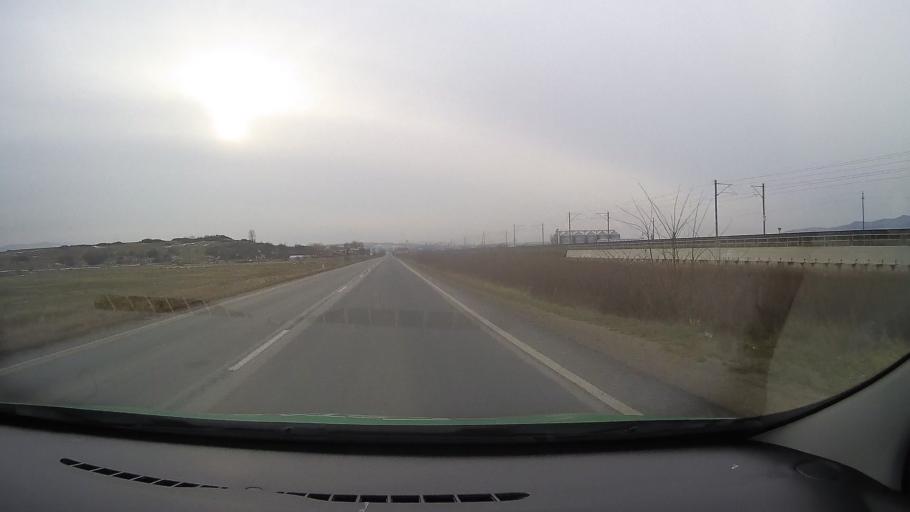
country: RO
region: Hunedoara
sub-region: Municipiul Orastie
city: Orastie
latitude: 45.8711
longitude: 23.2305
